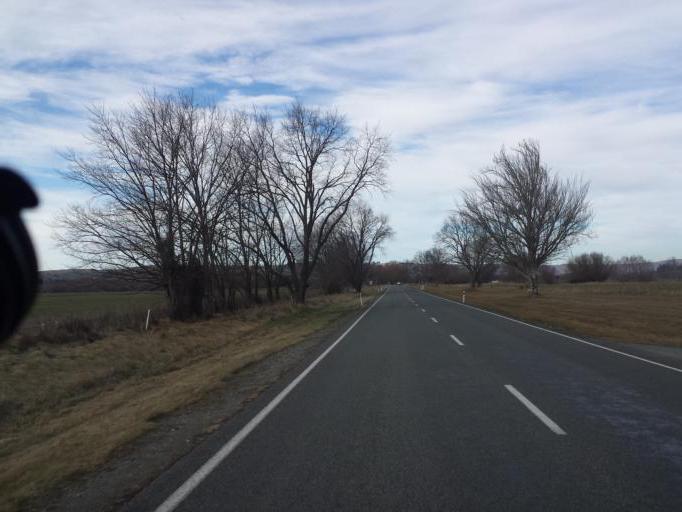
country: NZ
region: Canterbury
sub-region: Timaru District
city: Pleasant Point
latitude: -44.0802
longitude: 170.8051
